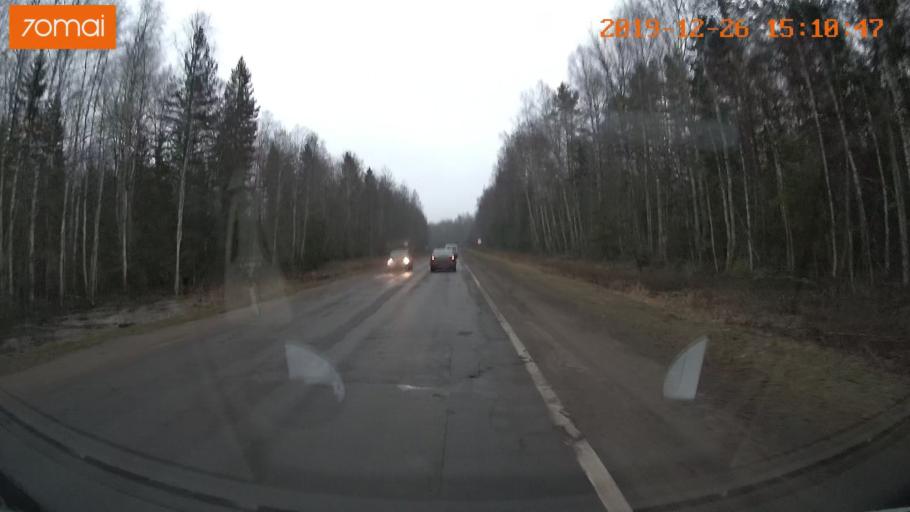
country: RU
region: Jaroslavl
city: Rybinsk
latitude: 58.1380
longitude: 38.8543
